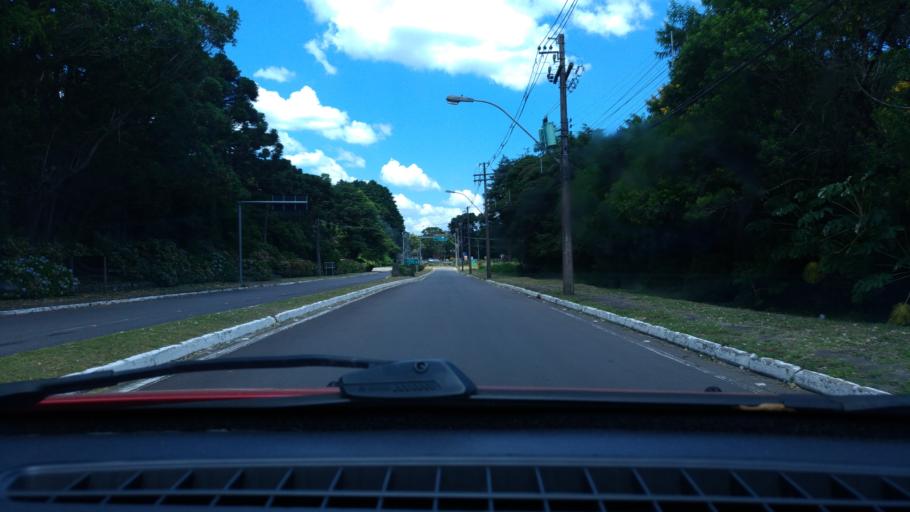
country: BR
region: Rio Grande do Sul
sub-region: Canela
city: Canela
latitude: -29.3585
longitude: -50.8271
